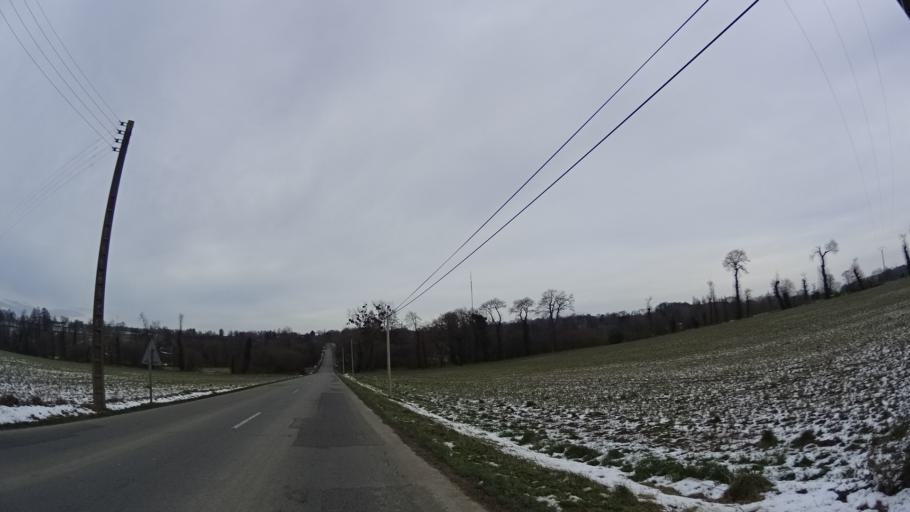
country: FR
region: Brittany
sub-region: Departement d'Ille-et-Vilaine
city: Irodouer
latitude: 48.2749
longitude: -1.9768
